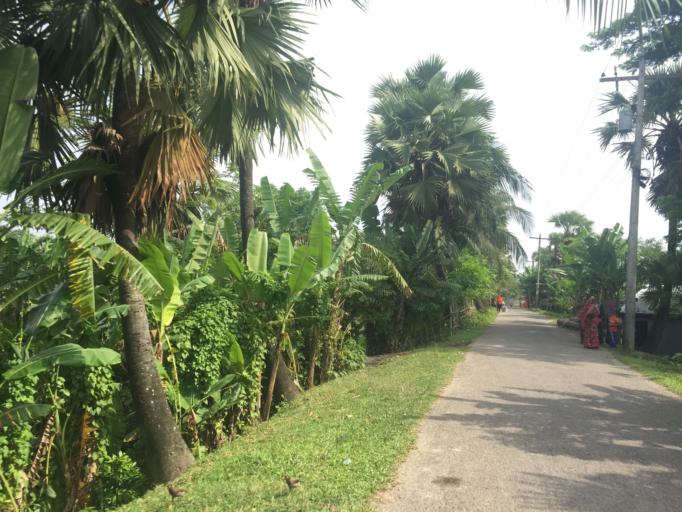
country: BD
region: Barisal
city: Mathba
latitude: 22.2328
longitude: 89.9156
